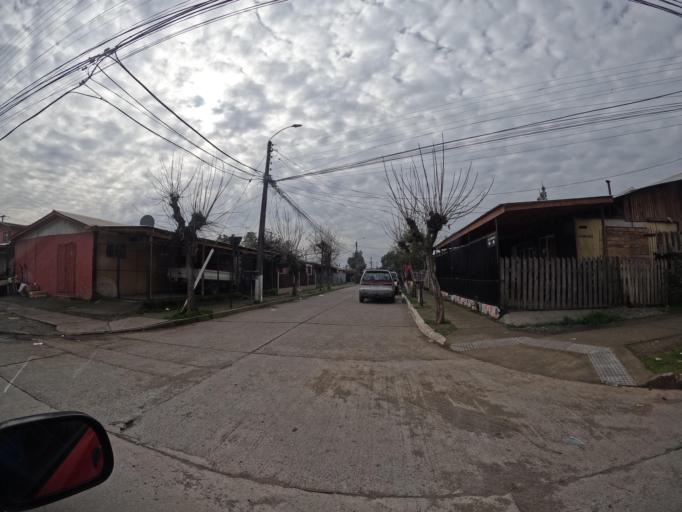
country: CL
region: Maule
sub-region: Provincia de Linares
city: Linares
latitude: -35.8349
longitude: -71.5980
